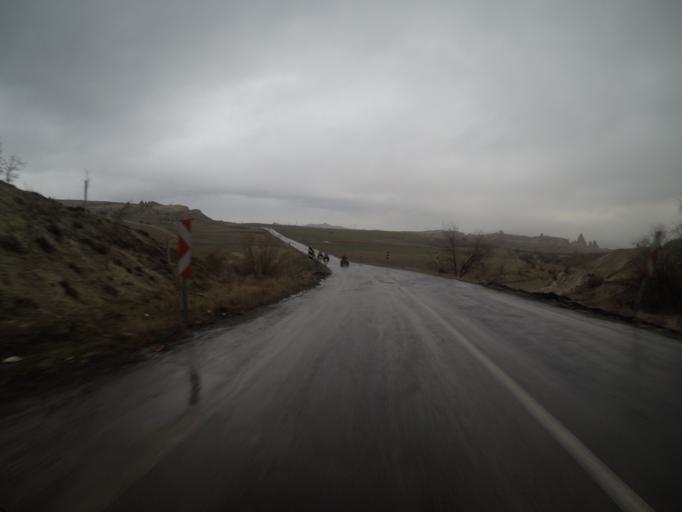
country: TR
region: Nevsehir
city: Goereme
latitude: 38.6643
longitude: 34.8291
